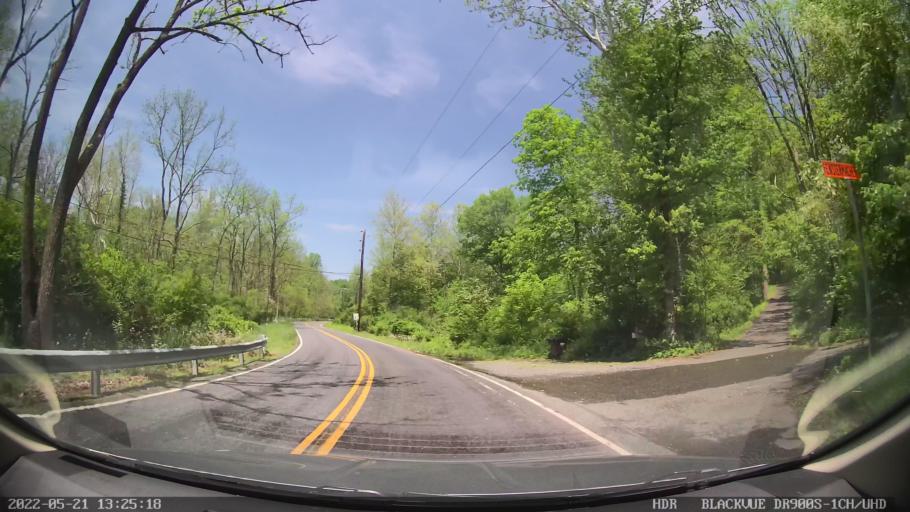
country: US
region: Pennsylvania
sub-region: Berks County
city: Bally
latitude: 40.3995
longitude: -75.6115
